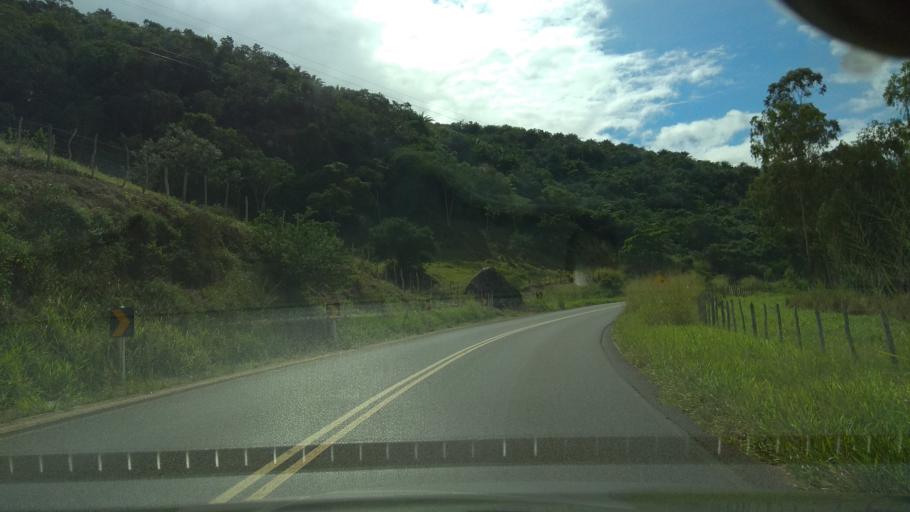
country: BR
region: Bahia
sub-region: Ubaira
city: Ubaira
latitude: -13.2603
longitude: -39.7040
